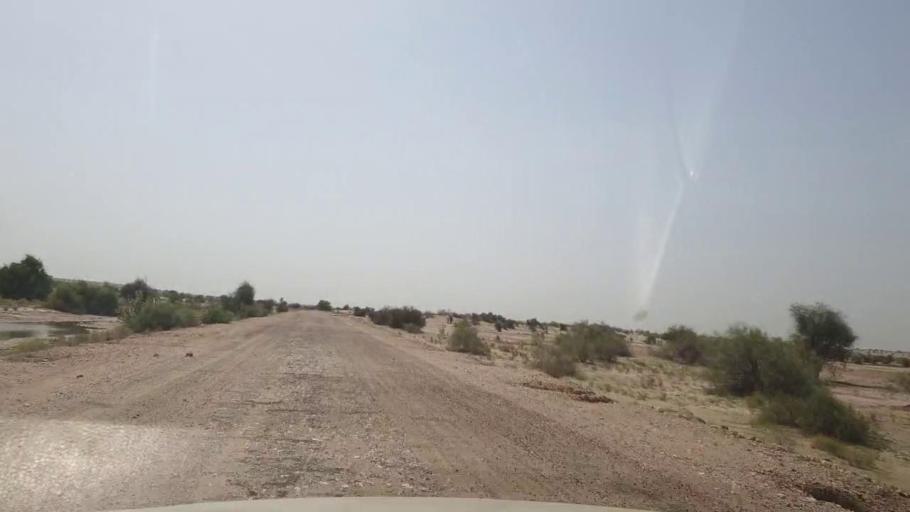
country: PK
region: Sindh
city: Khanpur
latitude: 27.4304
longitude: 69.2548
